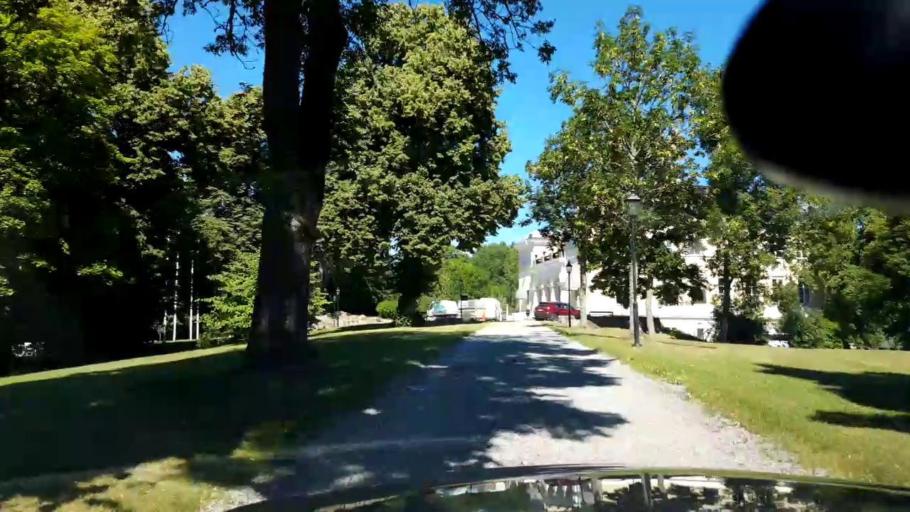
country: SE
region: Stockholm
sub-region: Sigtuna Kommun
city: Sigtuna
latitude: 59.6071
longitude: 17.6447
